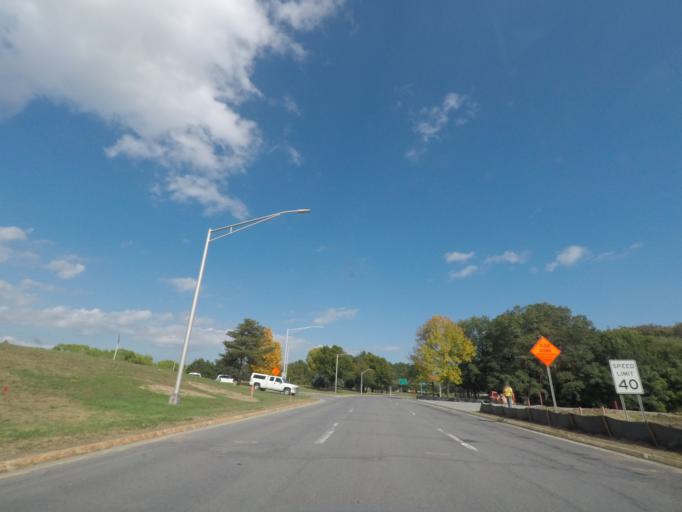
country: US
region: New York
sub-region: Albany County
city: Roessleville
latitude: 42.6828
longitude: -73.8151
